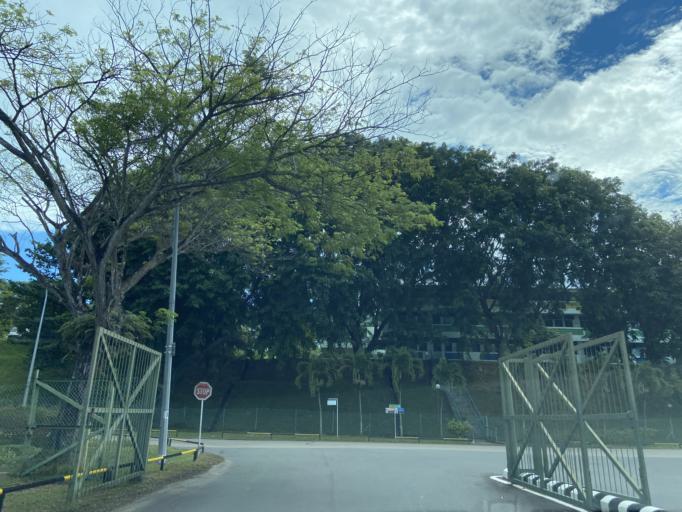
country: SG
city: Singapore
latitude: 1.0574
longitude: 104.0305
